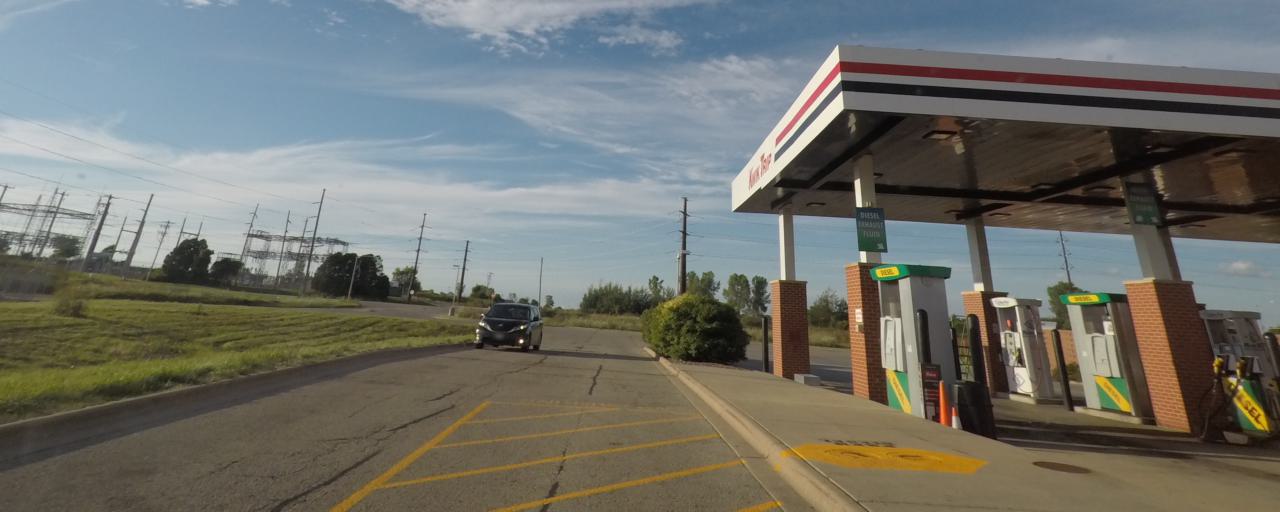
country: US
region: Wisconsin
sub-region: Dane County
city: Verona
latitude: 42.9713
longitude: -89.5136
